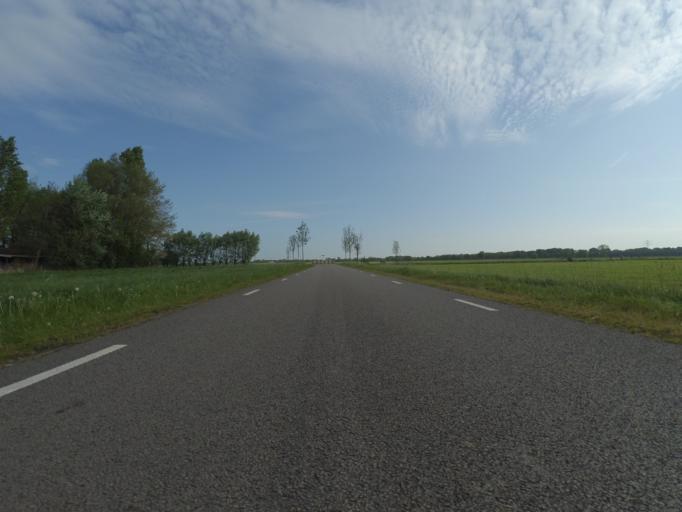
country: NL
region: Utrecht
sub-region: Gemeente Amersfoort
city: Hoogland
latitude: 52.1739
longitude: 5.3347
